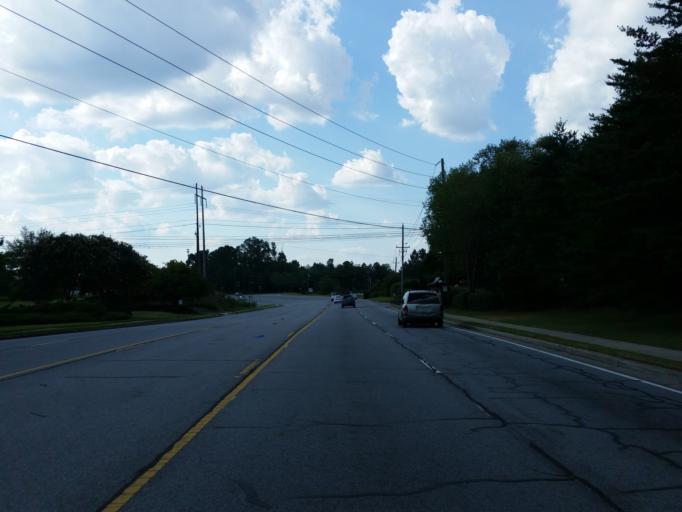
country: US
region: Georgia
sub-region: Gwinnett County
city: Duluth
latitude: 33.9538
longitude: -84.1038
